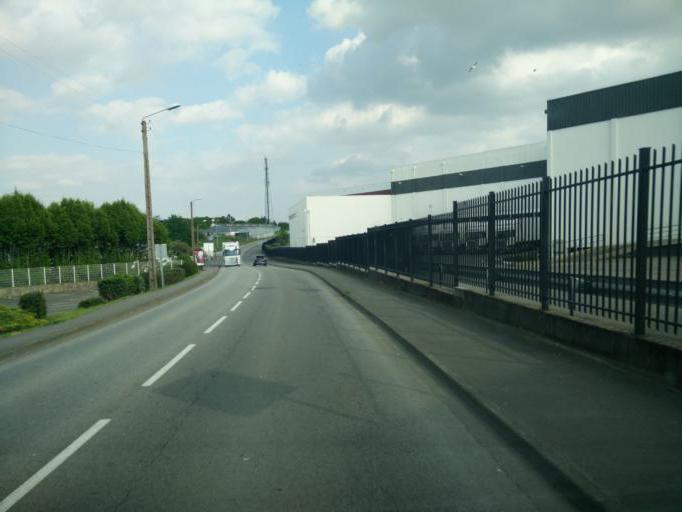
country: FR
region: Brittany
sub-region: Departement du Finistere
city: Quimperle
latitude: 47.8649
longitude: -3.5544
